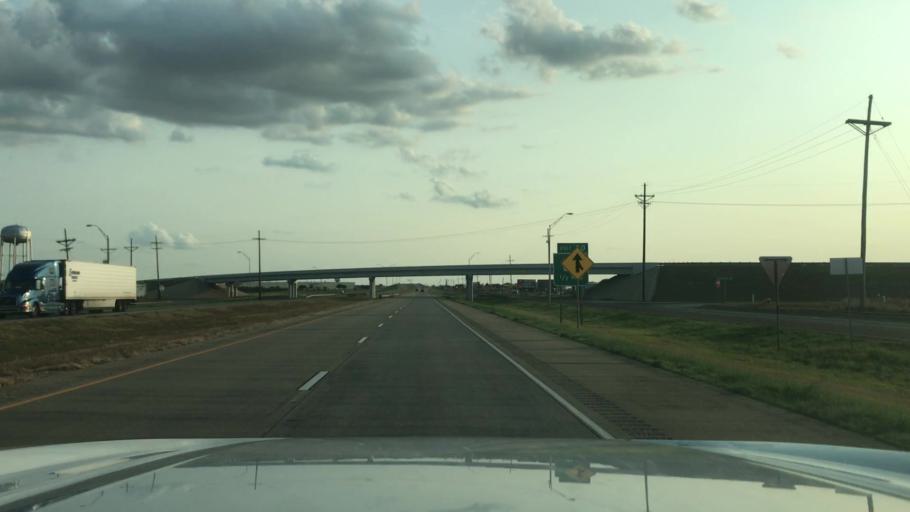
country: US
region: Texas
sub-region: Hale County
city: Seth Ward
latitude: 34.2207
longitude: -101.7240
